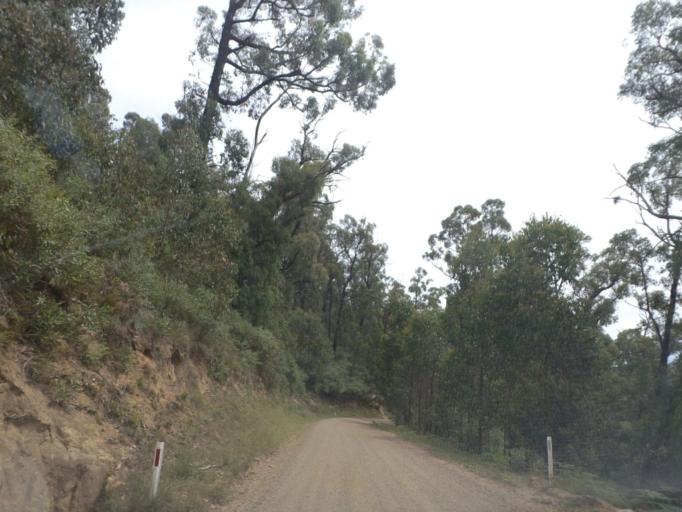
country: AU
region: Victoria
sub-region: Yarra Ranges
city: Healesville
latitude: -37.4475
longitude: 145.5781
